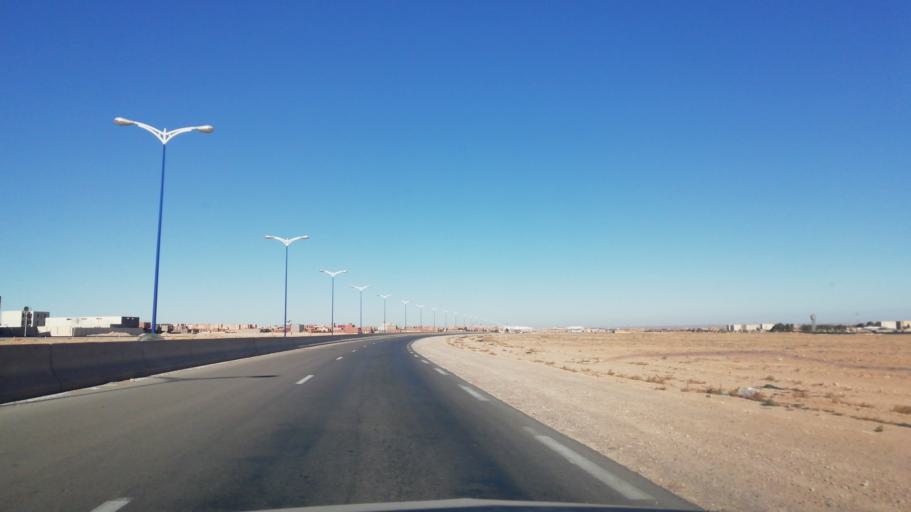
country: DZ
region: Wilaya de Naama
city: Naama
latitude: 33.5290
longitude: -0.2725
